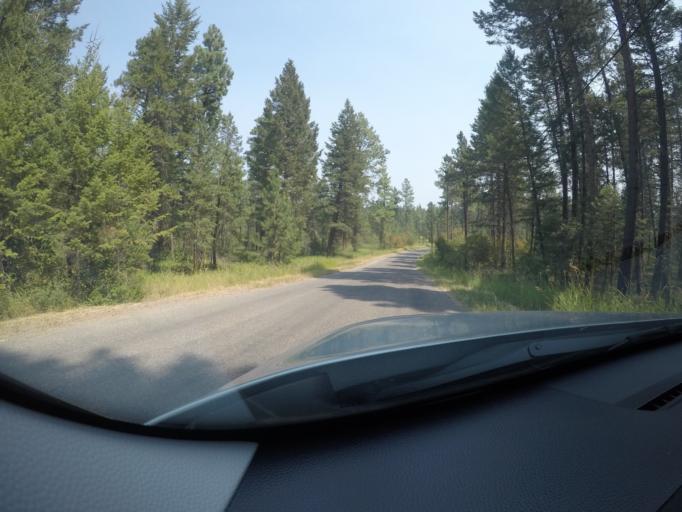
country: US
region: Montana
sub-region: Lake County
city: Polson
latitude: 47.7718
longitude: -114.1490
